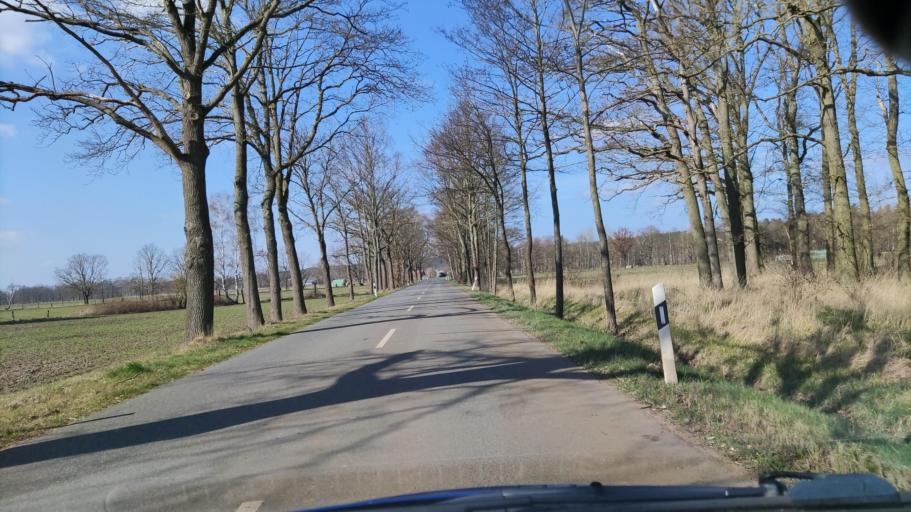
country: DE
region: Lower Saxony
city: Klein Gusborn
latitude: 53.0691
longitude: 11.2261
